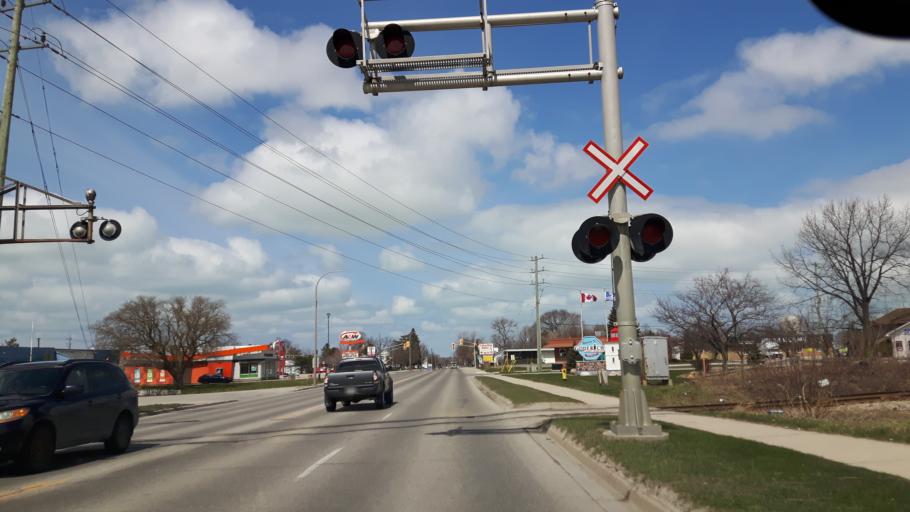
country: CA
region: Ontario
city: Goderich
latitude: 43.7320
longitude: -81.6919
